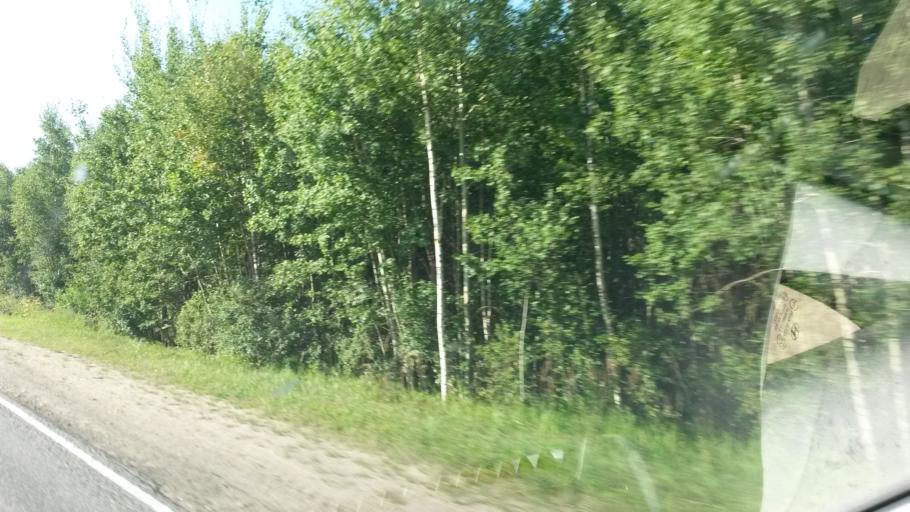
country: RU
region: Ivanovo
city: Novo-Talitsy
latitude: 57.0380
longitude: 40.7452
